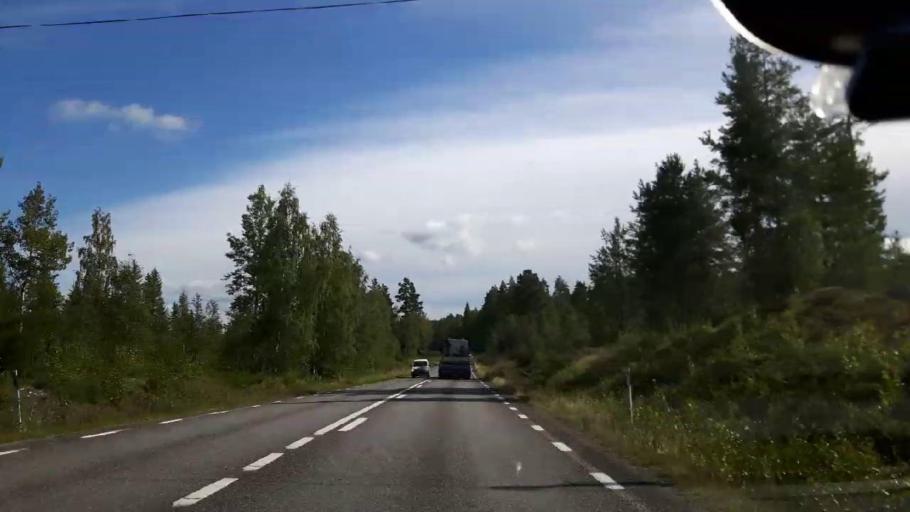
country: SE
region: Jaemtland
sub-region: Braecke Kommun
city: Braecke
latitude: 63.1905
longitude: 15.4515
